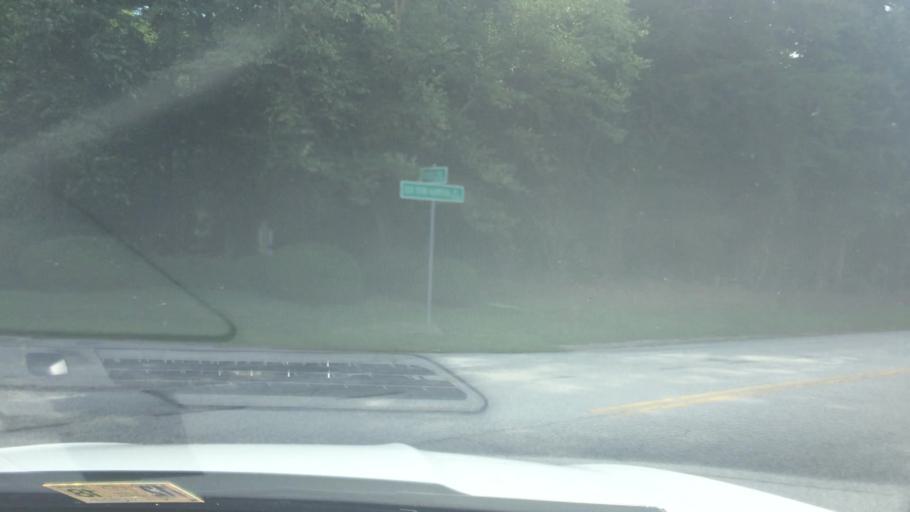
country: US
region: Virginia
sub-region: York County
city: Yorktown
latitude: 37.1976
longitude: -76.4848
